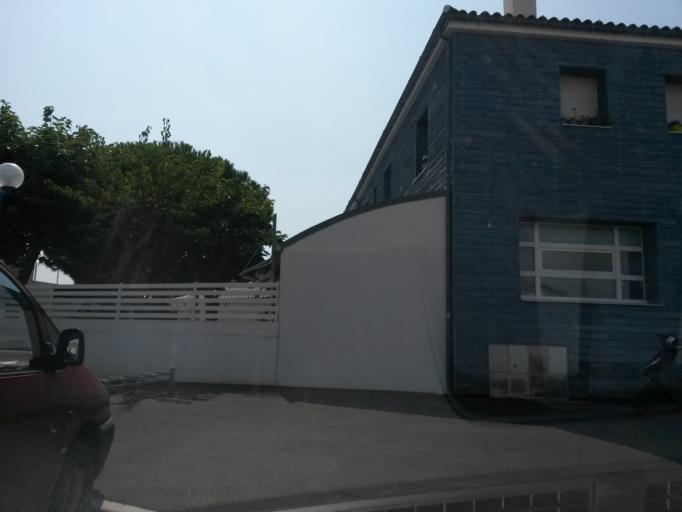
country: FR
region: Pays de la Loire
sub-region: Departement de la Vendee
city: La Tranche-sur-Mer
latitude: 46.3413
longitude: -1.4383
